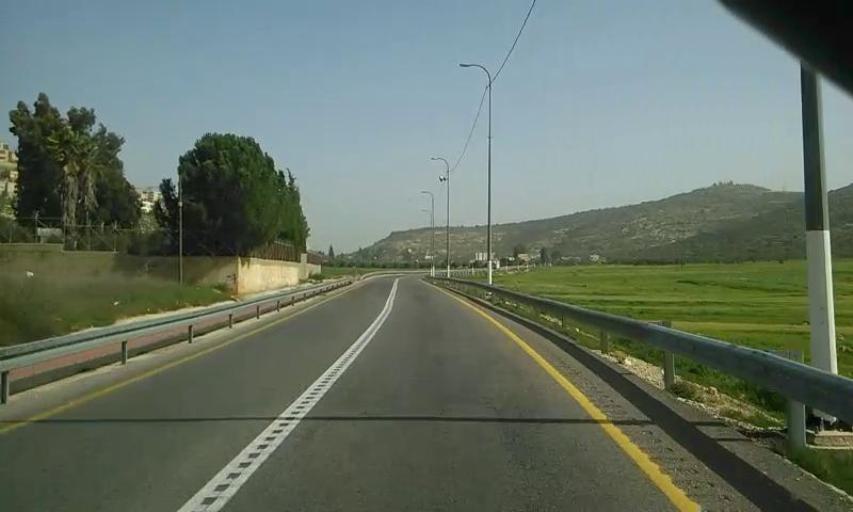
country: PS
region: West Bank
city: As Sawiyah
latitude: 32.0827
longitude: 35.2632
